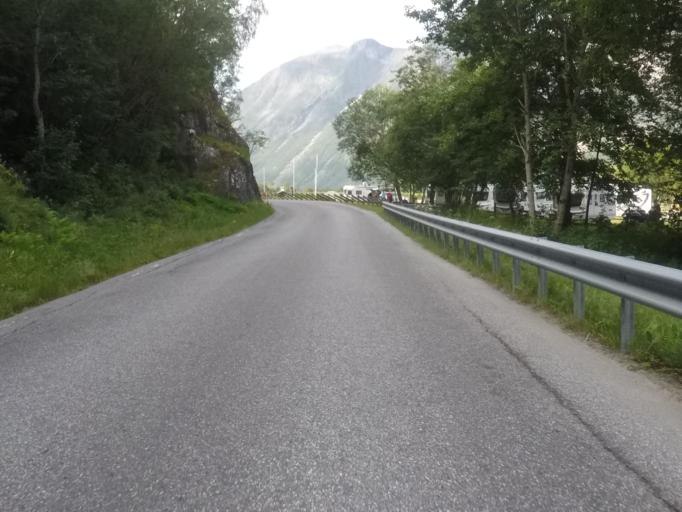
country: NO
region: More og Romsdal
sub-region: Rauma
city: Andalsnes
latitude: 62.5269
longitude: 7.7099
